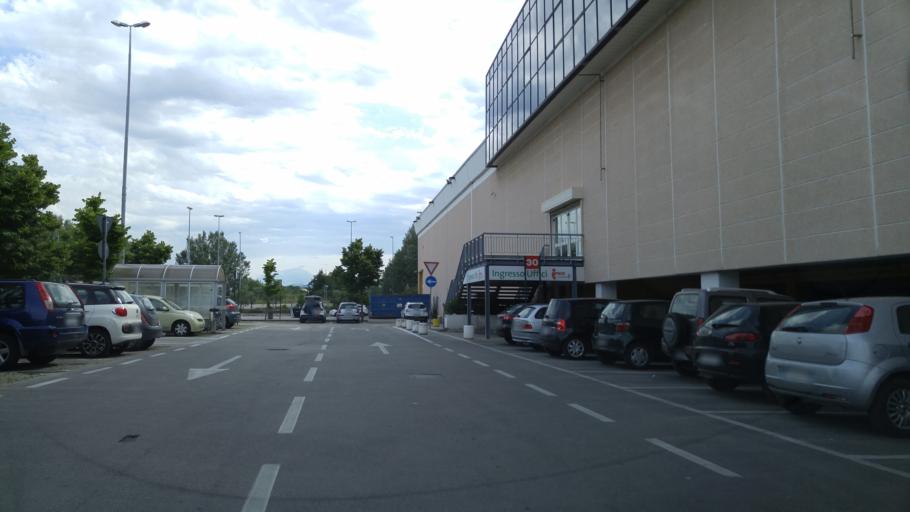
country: IT
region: The Marches
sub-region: Provincia di Pesaro e Urbino
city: Pesaro
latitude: 43.9044
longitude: 12.8694
